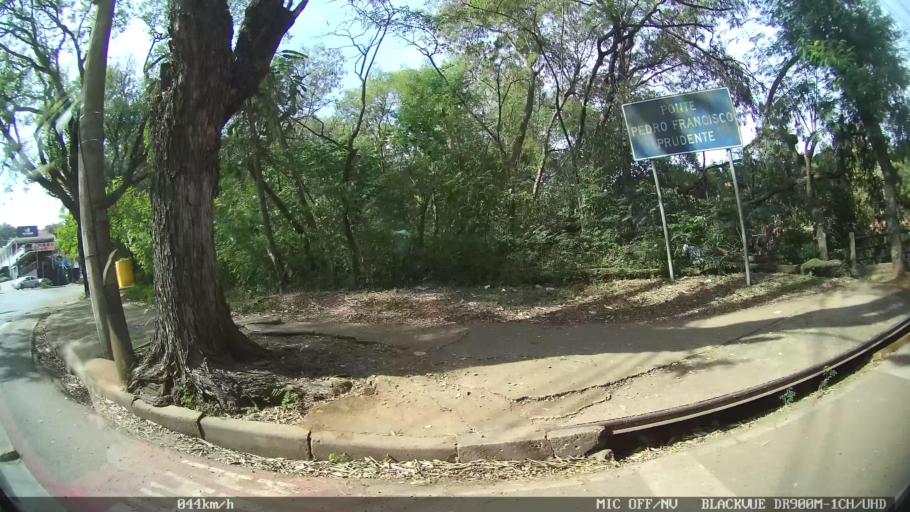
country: BR
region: Sao Paulo
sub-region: Piracicaba
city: Piracicaba
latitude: -22.7250
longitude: -47.6659
